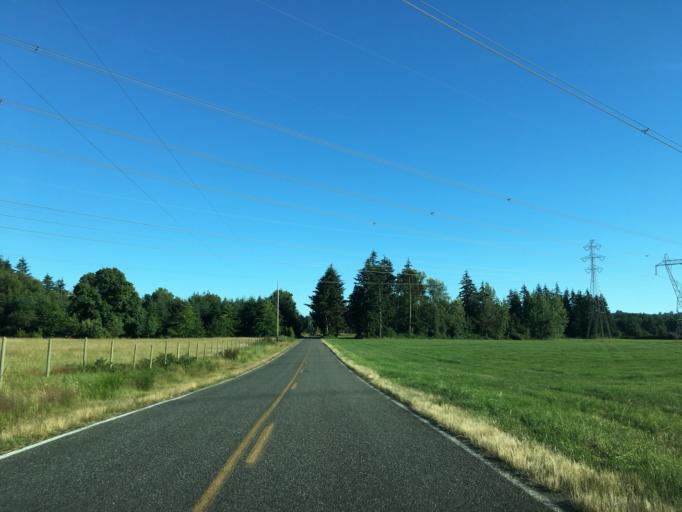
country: US
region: Washington
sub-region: Whatcom County
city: Ferndale
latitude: 48.9097
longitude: -122.6164
